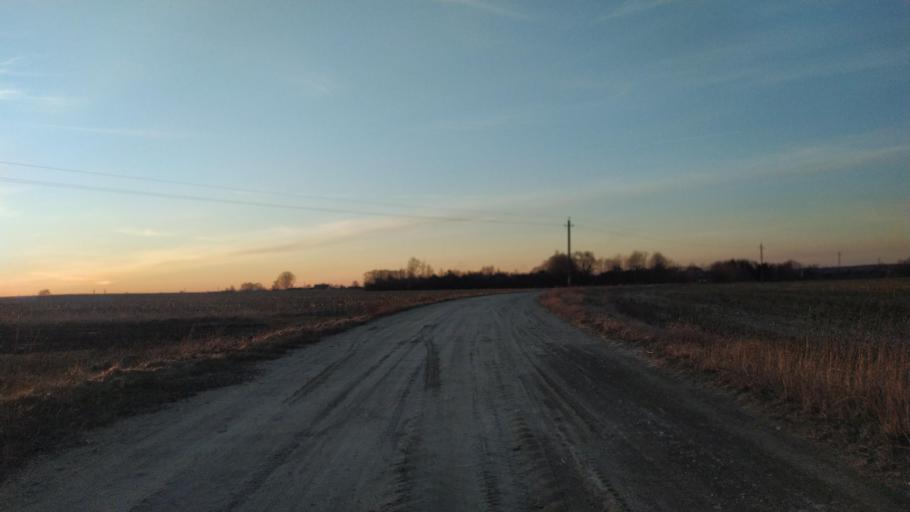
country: BY
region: Brest
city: Pruzhany
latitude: 52.5488
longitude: 24.2349
